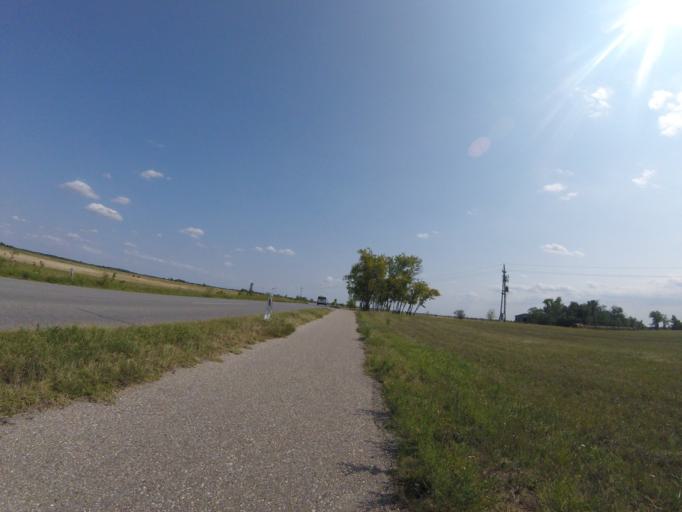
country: AT
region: Burgenland
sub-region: Politischer Bezirk Neusiedl am See
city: Apetlon
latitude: 47.7336
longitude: 16.8377
